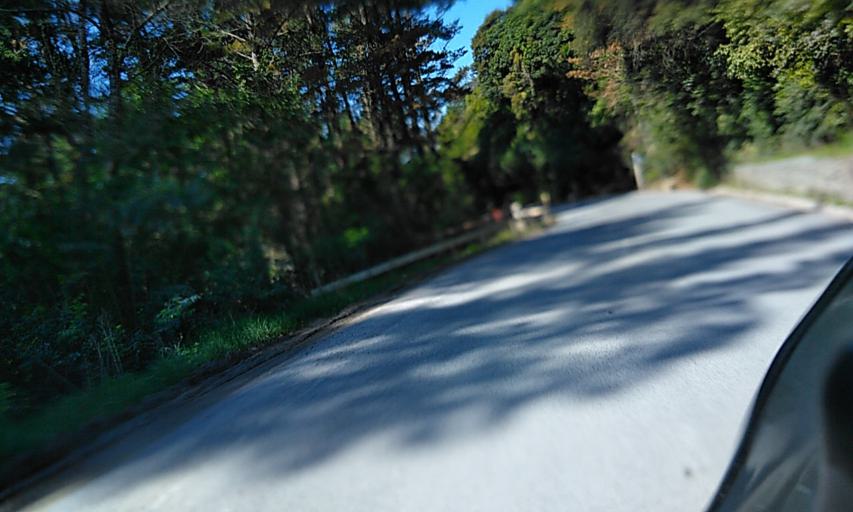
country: NZ
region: Gisborne
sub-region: Gisborne District
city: Gisborne
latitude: -38.3164
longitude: 178.1314
